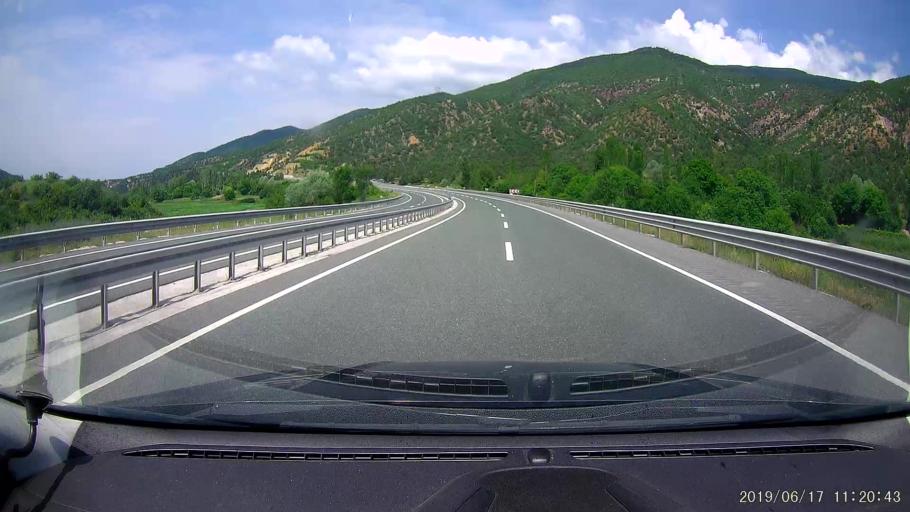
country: TR
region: Cankiri
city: Yaprakli
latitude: 40.9122
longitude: 33.8000
